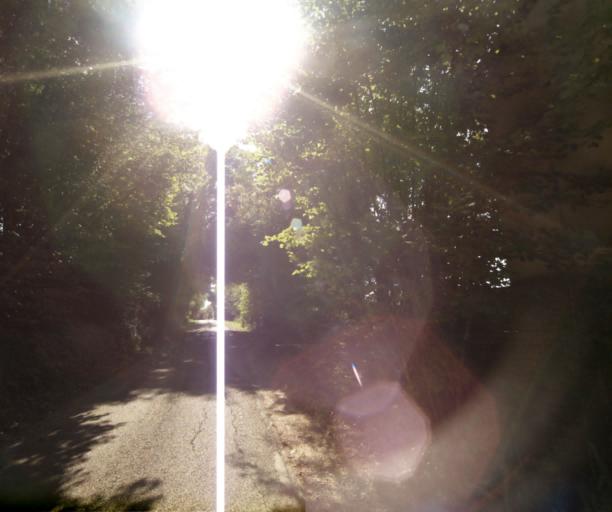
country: FR
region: Bourgogne
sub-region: Departement de Saone-et-Loire
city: Tournus
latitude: 46.5572
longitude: 4.8846
